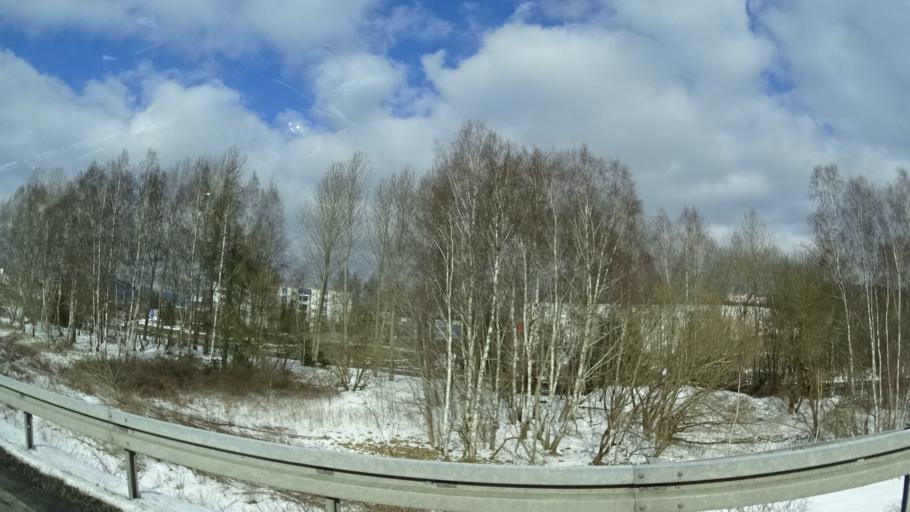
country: DE
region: Thuringia
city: Zella-Mehlis
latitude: 50.6418
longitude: 10.6868
